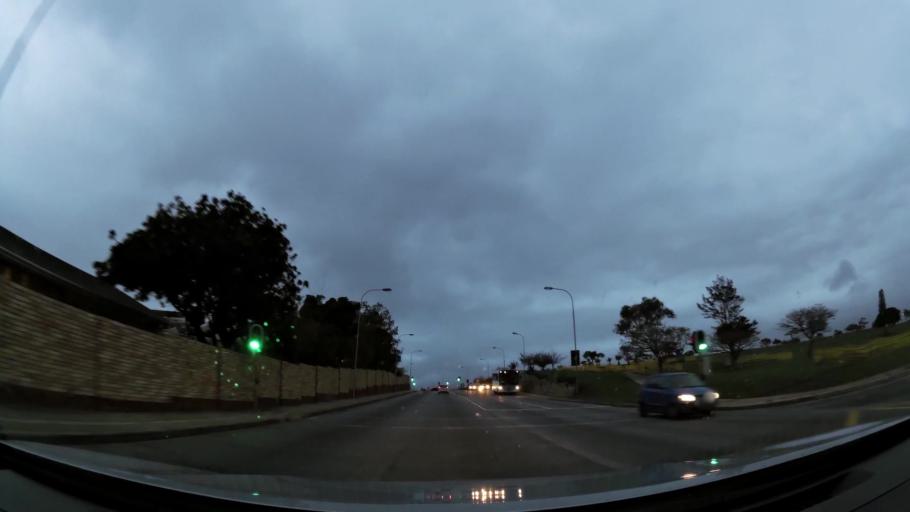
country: ZA
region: Eastern Cape
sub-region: Nelson Mandela Bay Metropolitan Municipality
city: Port Elizabeth
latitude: -33.9426
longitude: 25.5521
